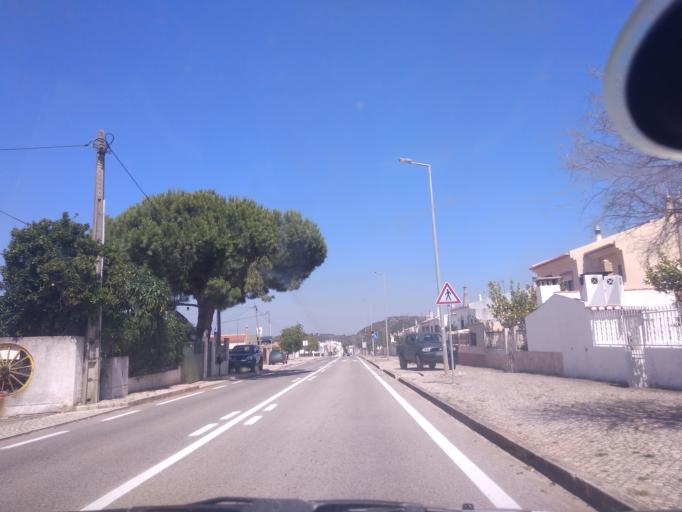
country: PT
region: Faro
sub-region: Lagos
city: Lagos
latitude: 37.1552
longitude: -8.7388
